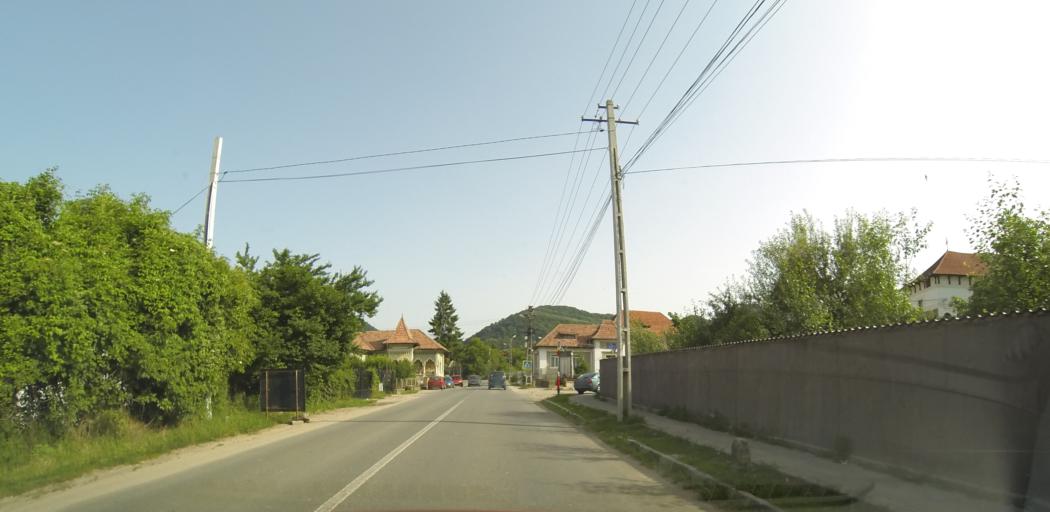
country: RO
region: Valcea
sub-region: Oras Baile Olanesti
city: Olanesti
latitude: 45.1811
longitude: 24.2578
